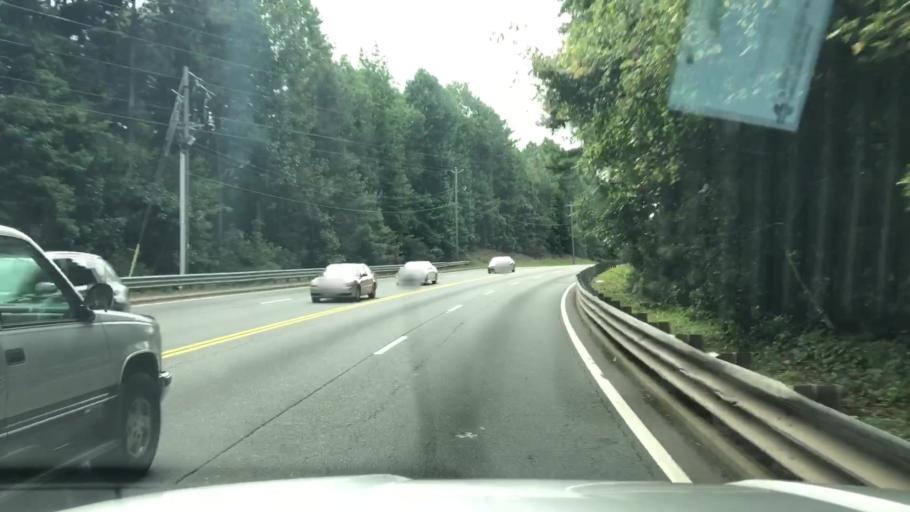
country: US
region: Georgia
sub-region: Fulton County
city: Roswell
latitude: 34.0110
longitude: -84.3022
